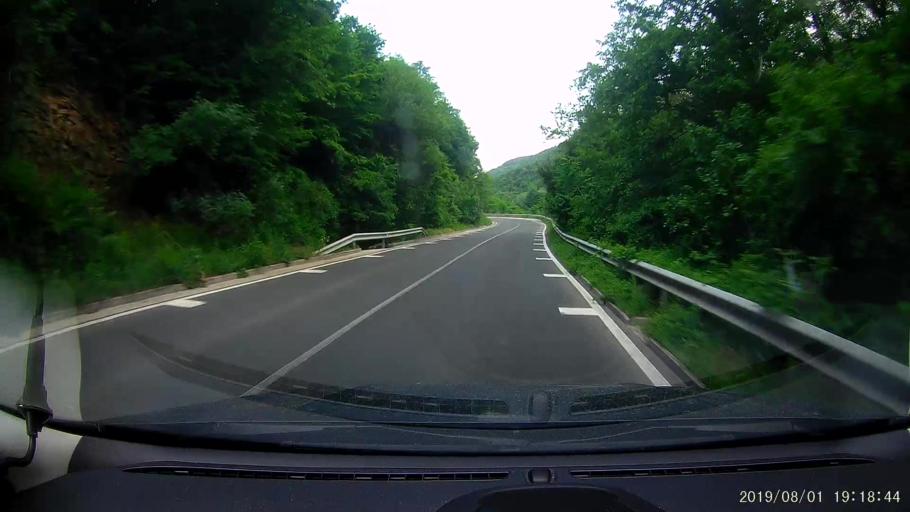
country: BG
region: Shumen
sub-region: Obshtina Smyadovo
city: Smyadovo
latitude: 42.9087
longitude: 26.9402
